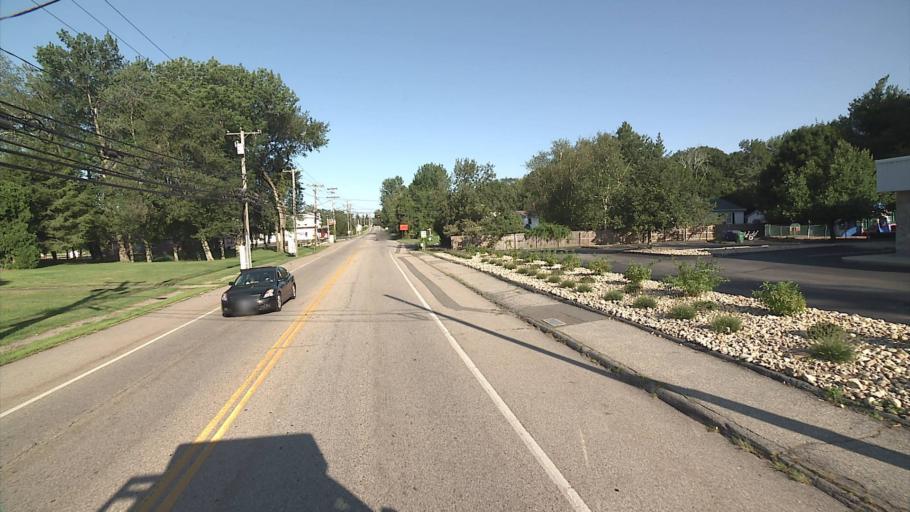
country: US
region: Connecticut
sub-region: New London County
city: Central Waterford
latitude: 41.3449
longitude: -72.1353
